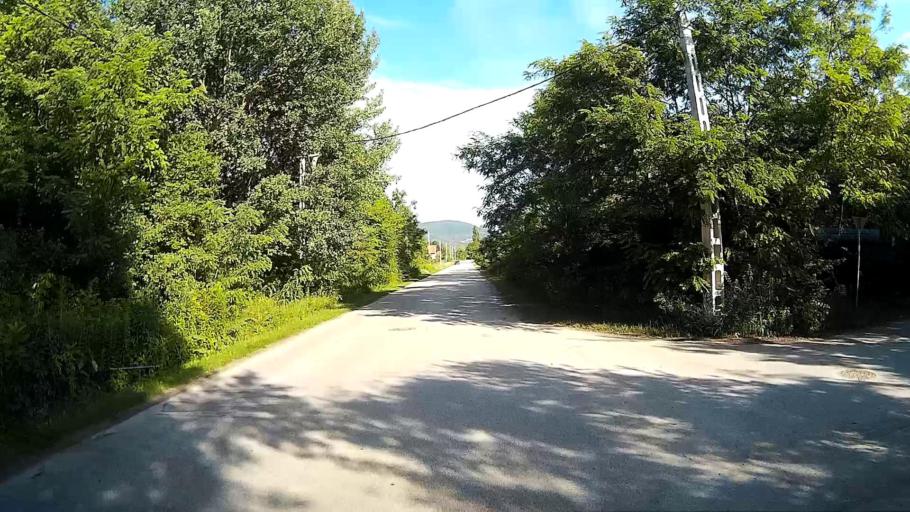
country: HU
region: Pest
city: God
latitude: 47.6810
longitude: 19.1114
